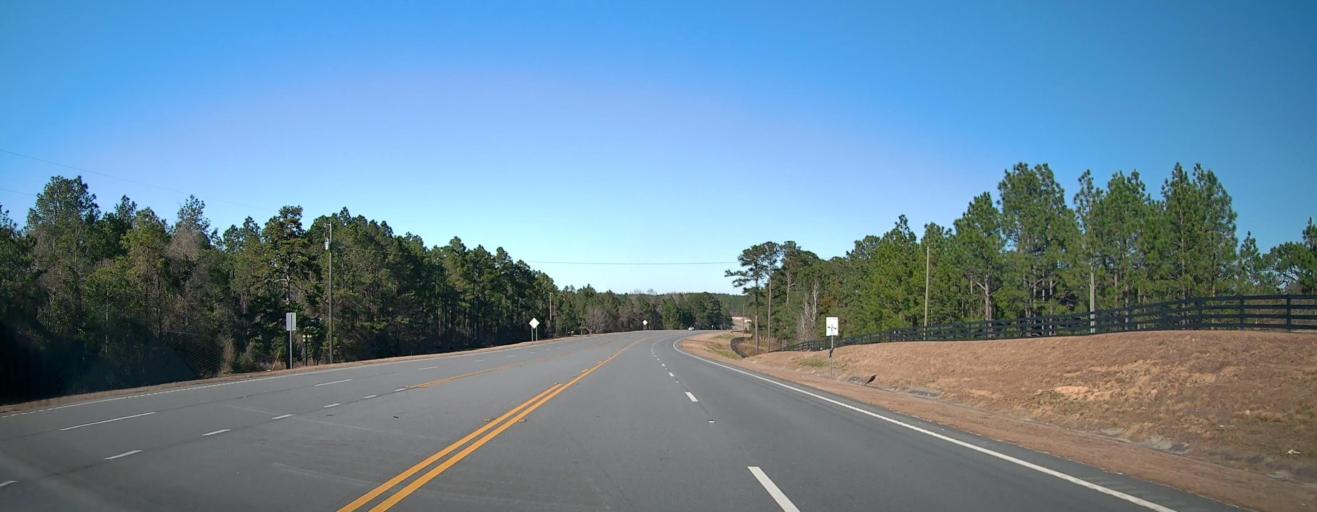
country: US
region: Georgia
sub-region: Taylor County
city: Butler
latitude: 32.5794
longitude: -84.2382
